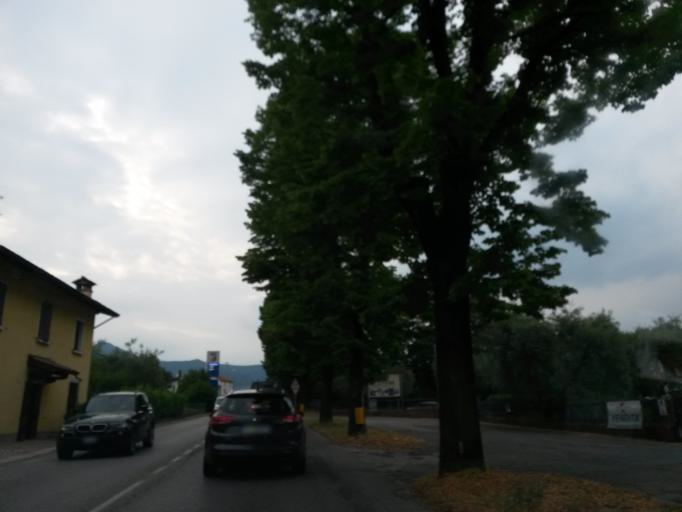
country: IT
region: Lombardy
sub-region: Provincia di Brescia
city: Cunettone-Villa
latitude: 45.5849
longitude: 10.5189
